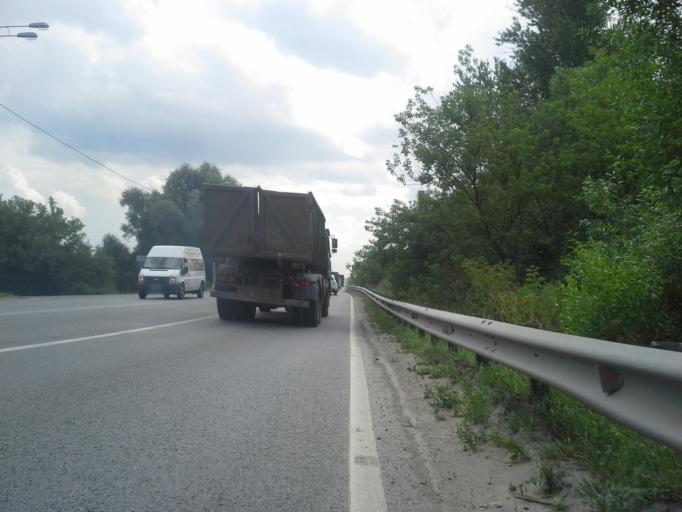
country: RU
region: Moskovskaya
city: Yam
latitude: 55.4959
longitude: 37.7502
